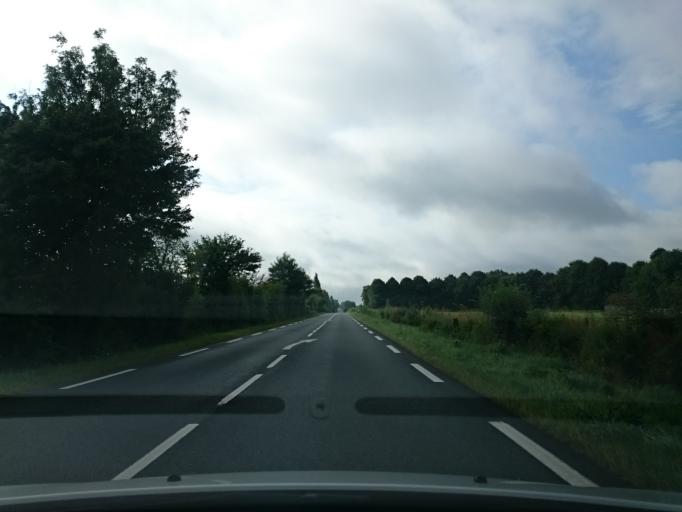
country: FR
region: Lower Normandy
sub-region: Departement du Calvados
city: Cambremer
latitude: 49.1278
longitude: 0.0047
